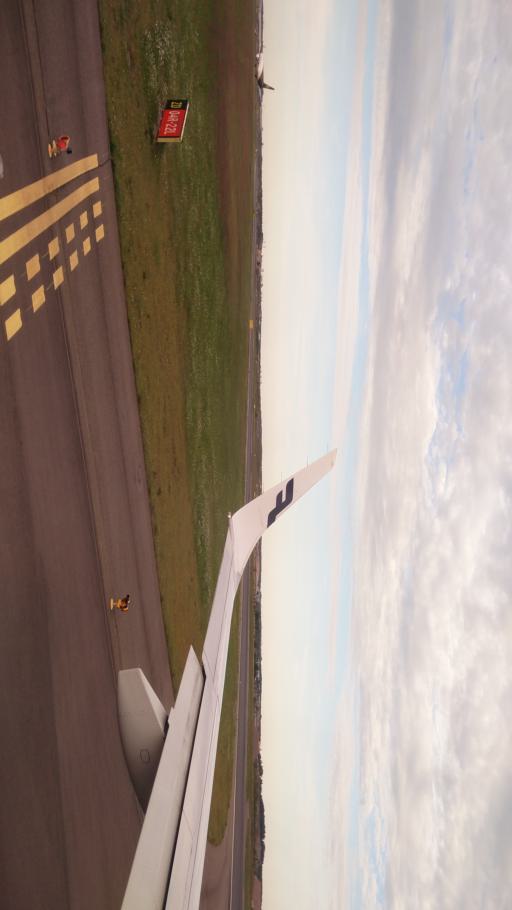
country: FI
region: Uusimaa
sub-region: Helsinki
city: Vantaa
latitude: 60.3235
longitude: 24.9660
